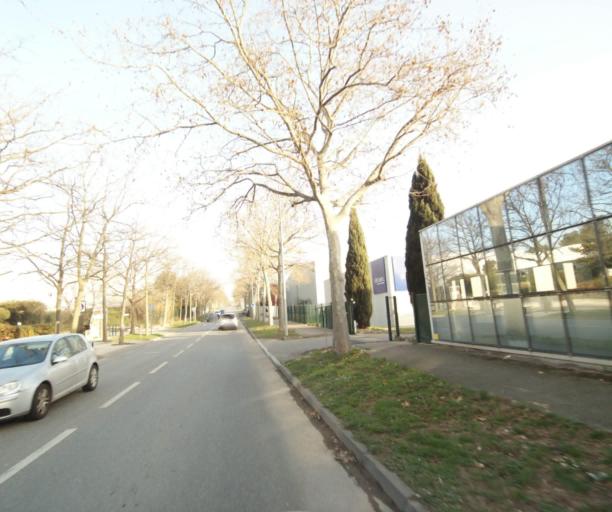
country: FR
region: Provence-Alpes-Cote d'Azur
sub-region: Departement des Bouches-du-Rhone
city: Saint-Victoret
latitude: 43.4230
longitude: 5.2604
